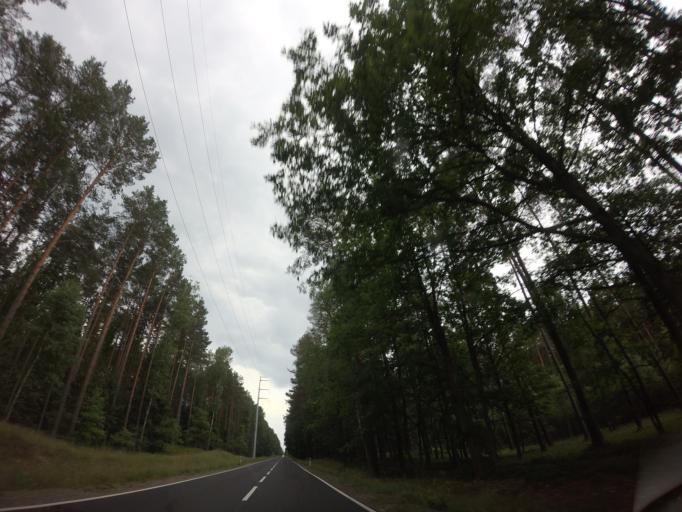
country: PL
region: West Pomeranian Voivodeship
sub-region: Powiat drawski
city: Czaplinek
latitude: 53.4817
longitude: 16.2278
